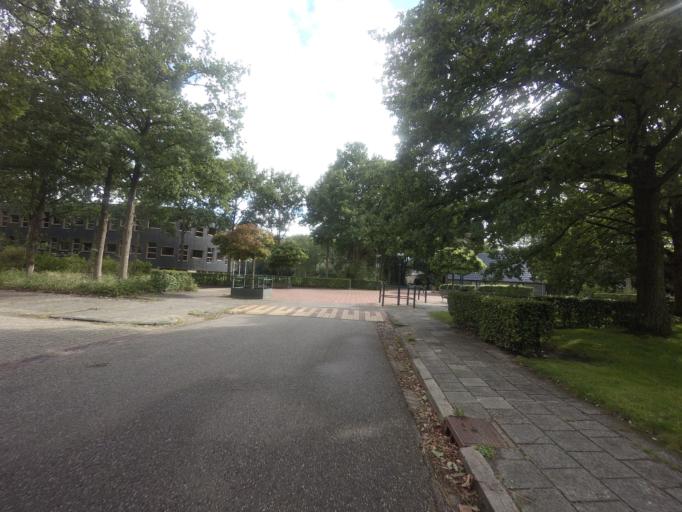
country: NL
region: Friesland
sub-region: Gemeente Heerenveen
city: Jubbega
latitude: 52.9957
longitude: 6.2930
